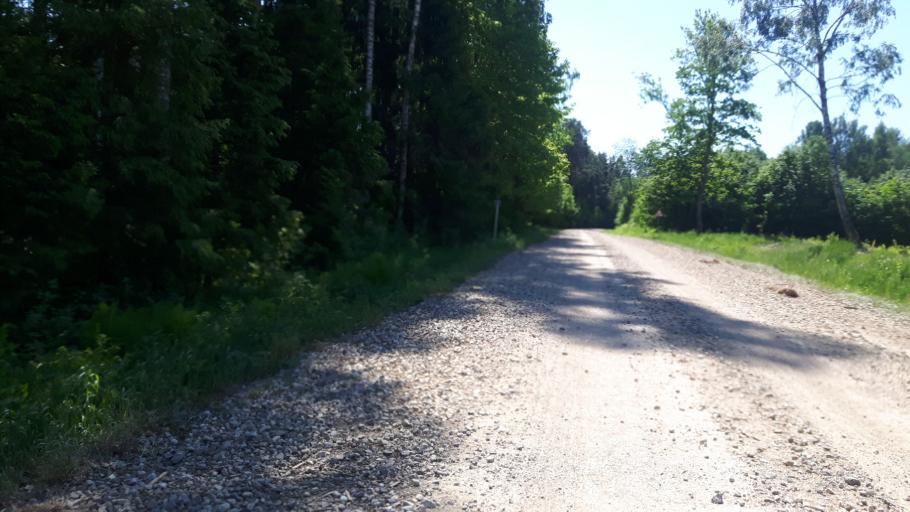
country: EE
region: Paernumaa
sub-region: Tootsi vald
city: Tootsi
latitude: 58.5101
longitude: 24.9085
